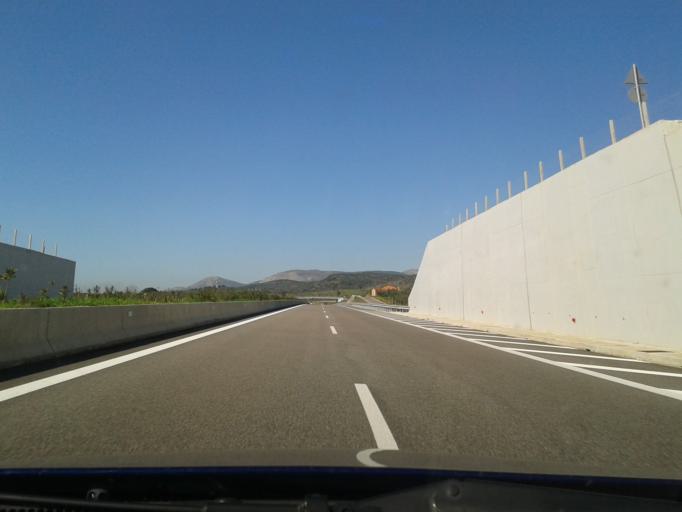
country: GR
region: West Greece
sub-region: Nomos Aitolias kai Akarnanias
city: Mesolongi
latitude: 38.3884
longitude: 21.4821
